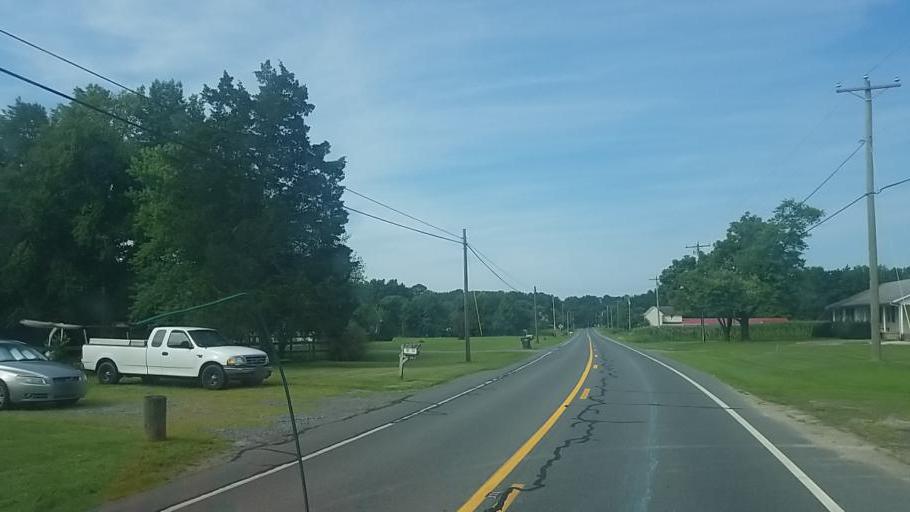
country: US
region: Delaware
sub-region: Sussex County
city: Selbyville
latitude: 38.5250
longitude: -75.2197
